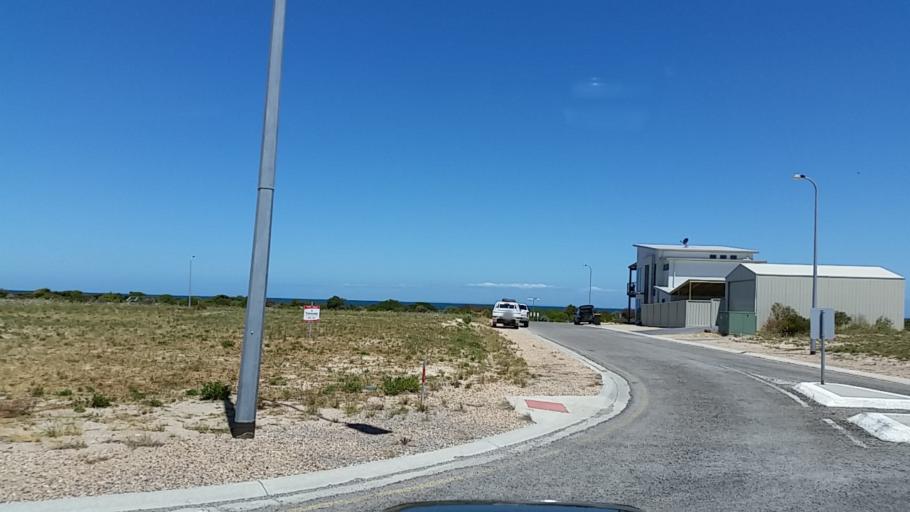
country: AU
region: South Australia
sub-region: Yorke Peninsula
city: Honiton
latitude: -35.2324
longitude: 136.9843
